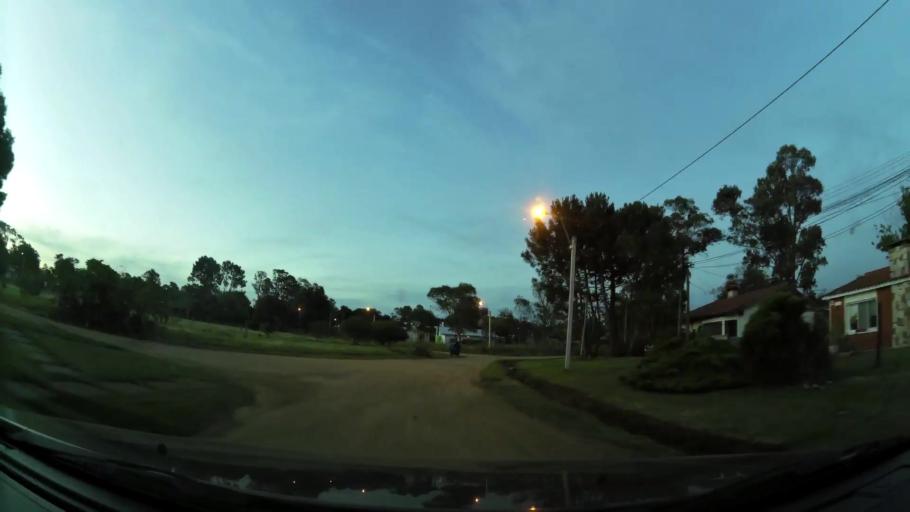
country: UY
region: Canelones
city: Atlantida
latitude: -34.7723
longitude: -55.7496
